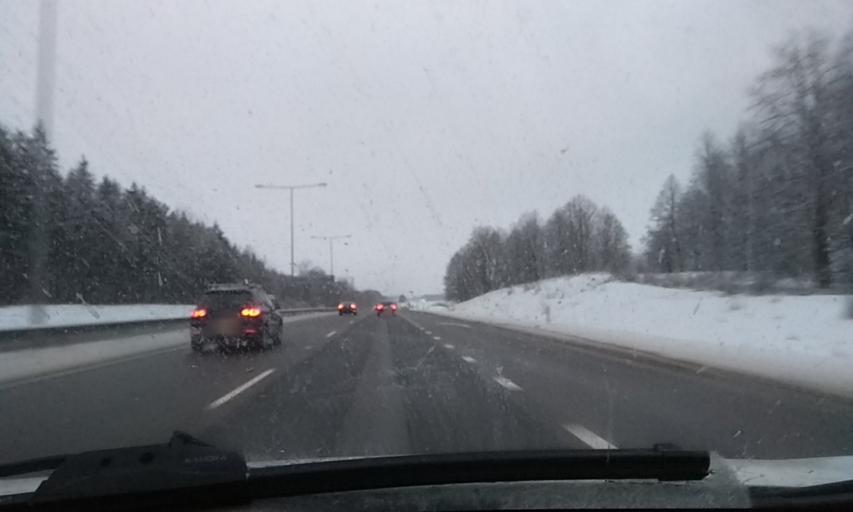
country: LT
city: Ziezmariai
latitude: 54.8199
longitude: 24.4210
